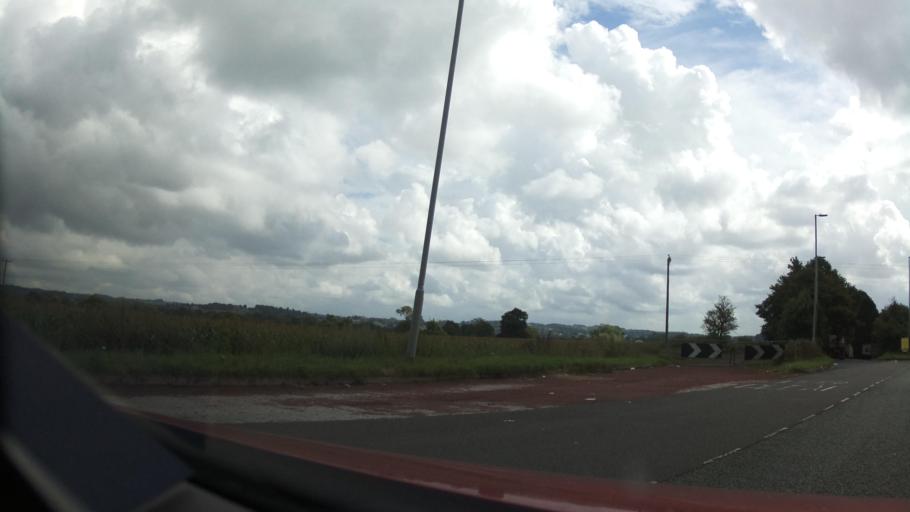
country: GB
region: England
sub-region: Staffordshire
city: Barlaston
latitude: 52.9556
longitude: -2.1927
